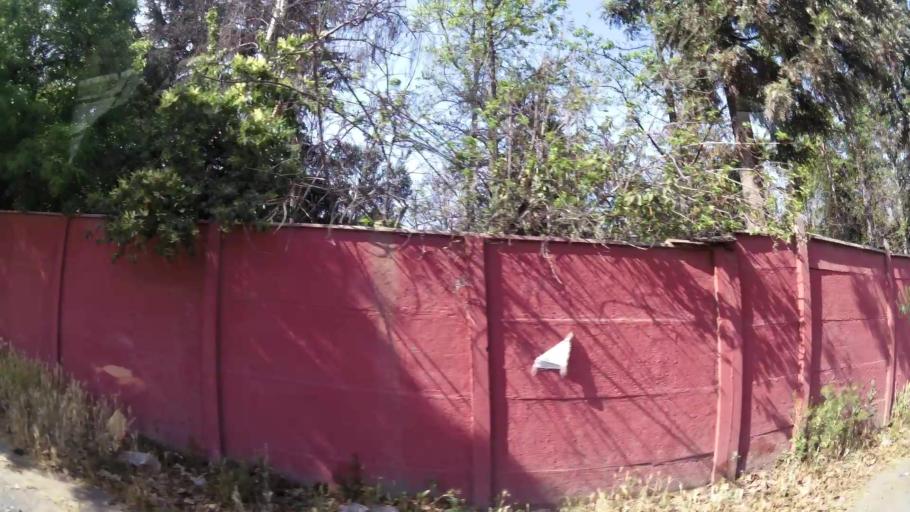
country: CL
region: Santiago Metropolitan
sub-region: Provincia de Santiago
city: Villa Presidente Frei, Nunoa, Santiago, Chile
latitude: -33.5283
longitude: -70.5753
